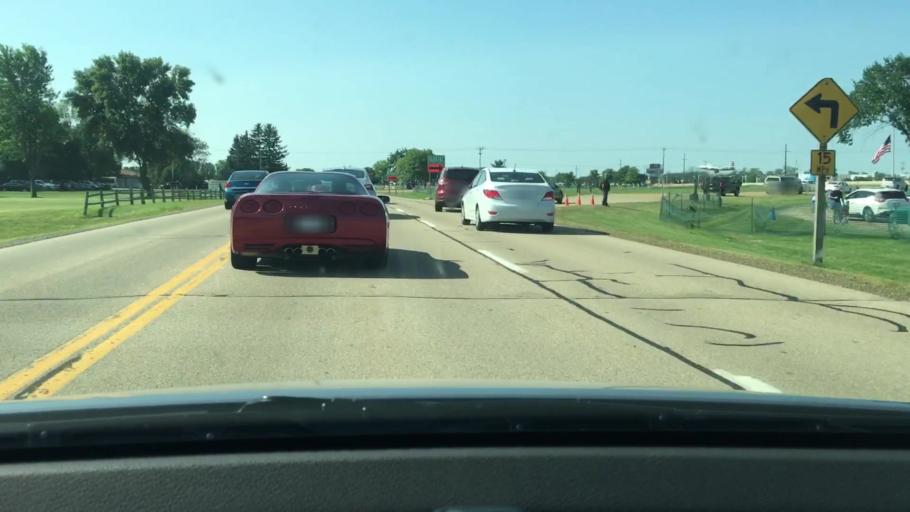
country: US
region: Wisconsin
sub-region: Winnebago County
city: Oshkosh
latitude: 43.9835
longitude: -88.5802
